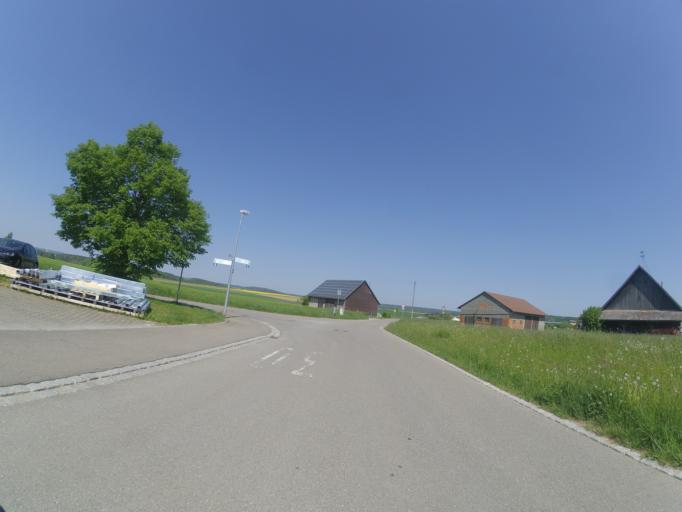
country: DE
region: Baden-Wuerttemberg
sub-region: Tuebingen Region
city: Blaubeuren
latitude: 48.4640
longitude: 9.8423
